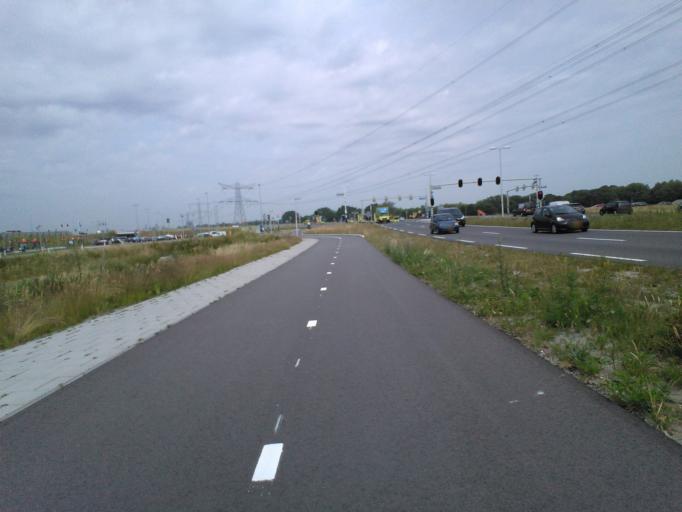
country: NL
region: North Holland
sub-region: Gemeente Weesp
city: Weesp
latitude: 52.3281
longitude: 5.0523
